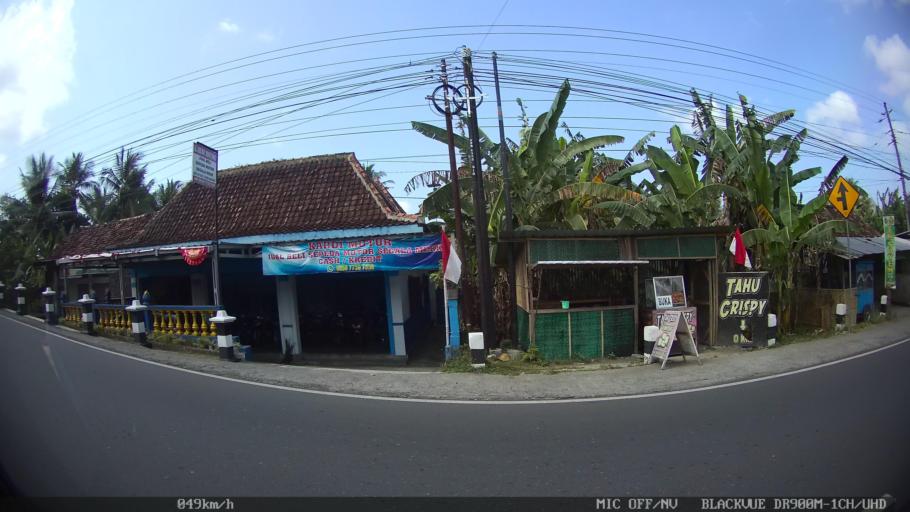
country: ID
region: Daerah Istimewa Yogyakarta
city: Srandakan
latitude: -7.8932
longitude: 110.1396
